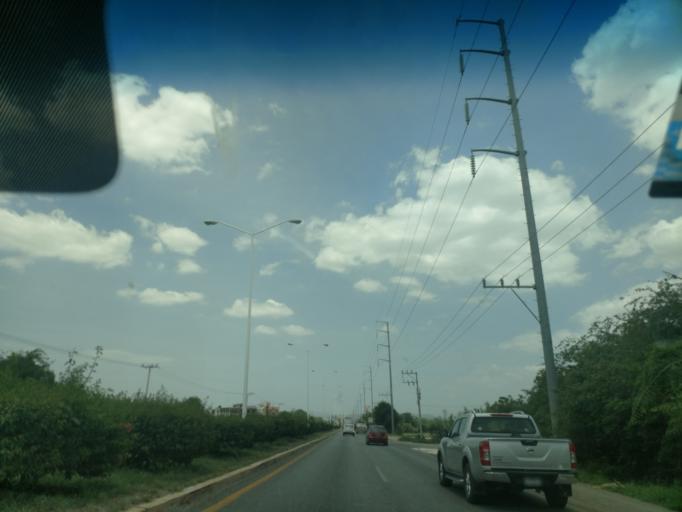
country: MX
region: San Luis Potosi
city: Rio Verde
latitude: 21.9226
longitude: -99.9846
